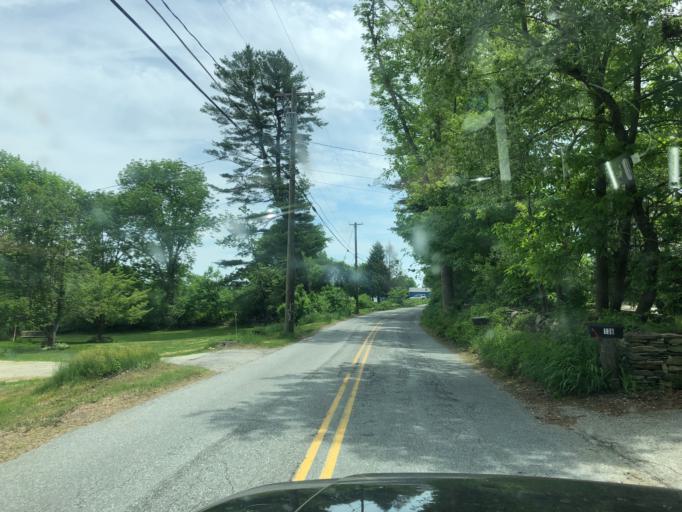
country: US
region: Connecticut
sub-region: Windham County
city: Thompson
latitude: 41.9708
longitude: -71.8364
